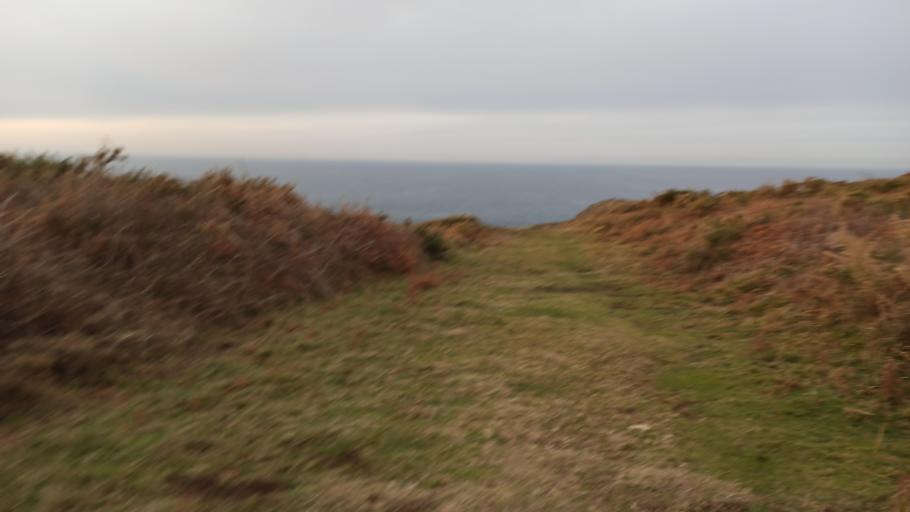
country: ES
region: Galicia
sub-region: Provincia da Coruna
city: A Coruna
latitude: 43.3961
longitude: -8.3426
